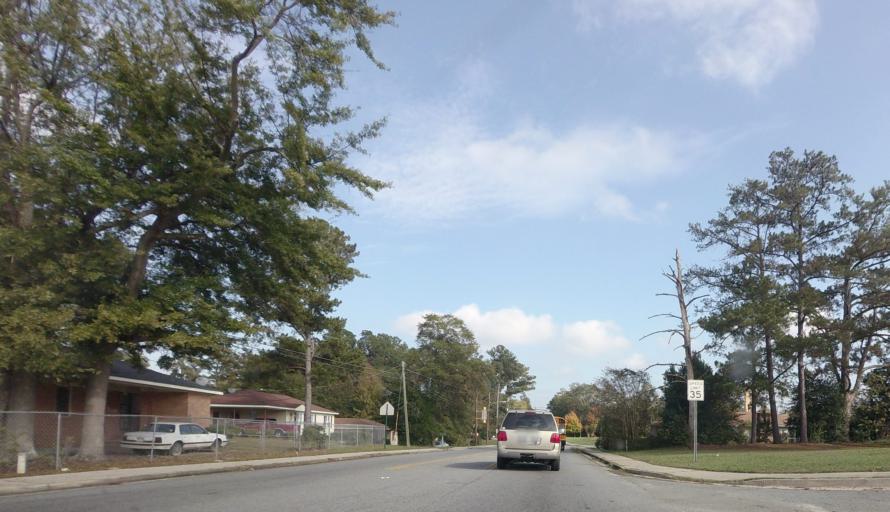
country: US
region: Georgia
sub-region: Bibb County
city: Macon
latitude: 32.8060
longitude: -83.6712
